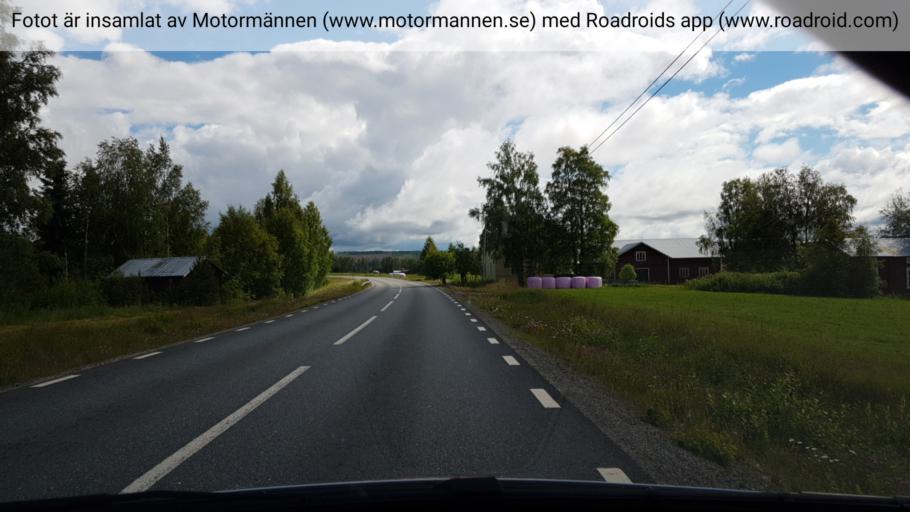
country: SE
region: Vaesterbotten
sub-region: Bjurholms Kommun
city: Bjurholm
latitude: 64.3054
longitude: 19.1650
